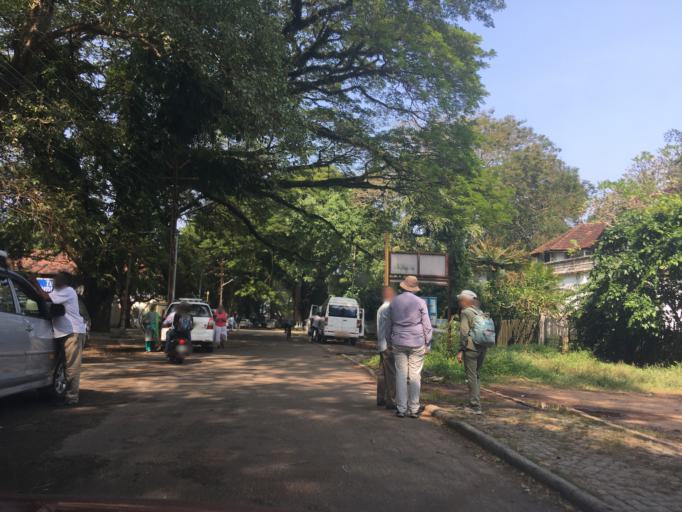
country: IN
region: Kerala
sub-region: Ernakulam
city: Cochin
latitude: 9.9667
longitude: 76.2410
